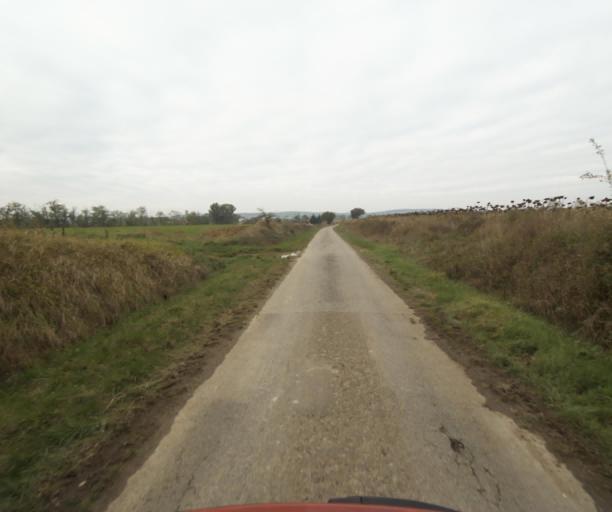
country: FR
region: Midi-Pyrenees
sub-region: Departement de la Haute-Garonne
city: Launac
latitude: 43.8046
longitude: 1.1785
